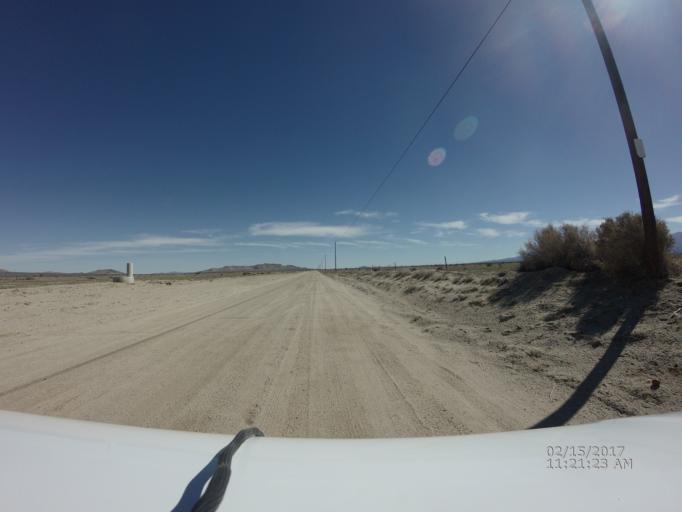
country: US
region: California
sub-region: Los Angeles County
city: Littlerock
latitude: 34.5870
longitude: -117.9292
